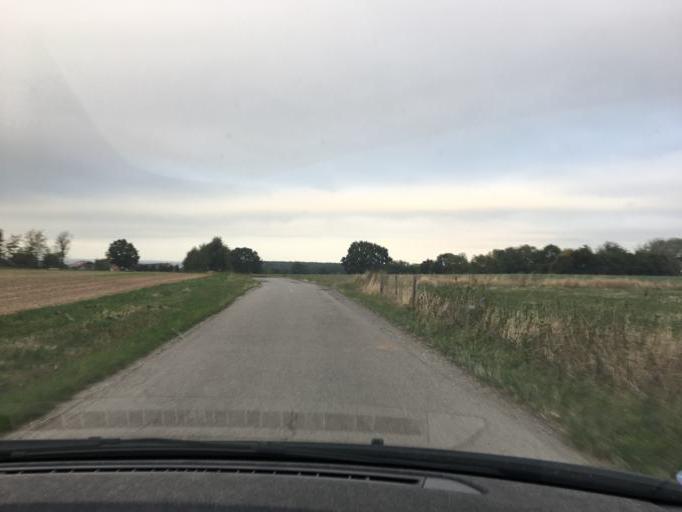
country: DE
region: North Rhine-Westphalia
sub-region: Regierungsbezirk Koln
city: Kreuzau
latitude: 50.7362
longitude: 6.4622
